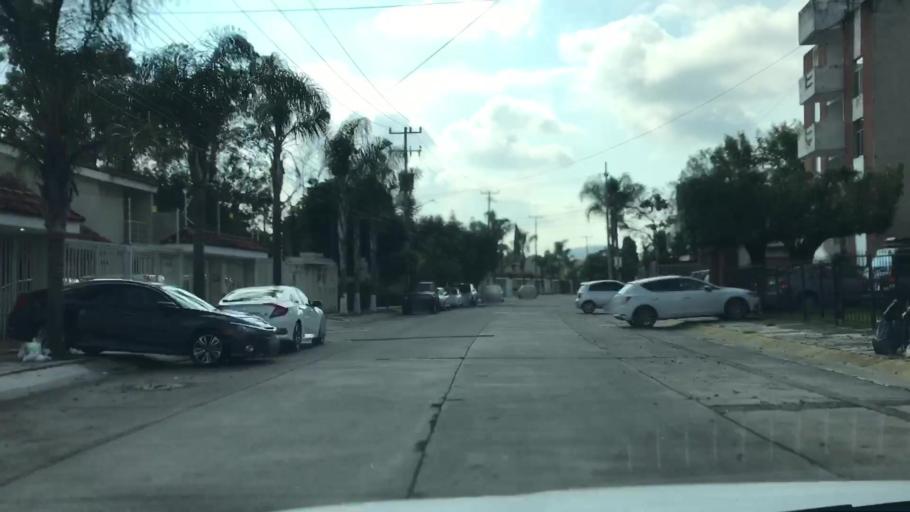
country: MX
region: Jalisco
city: Guadalajara
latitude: 20.6373
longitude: -103.4308
